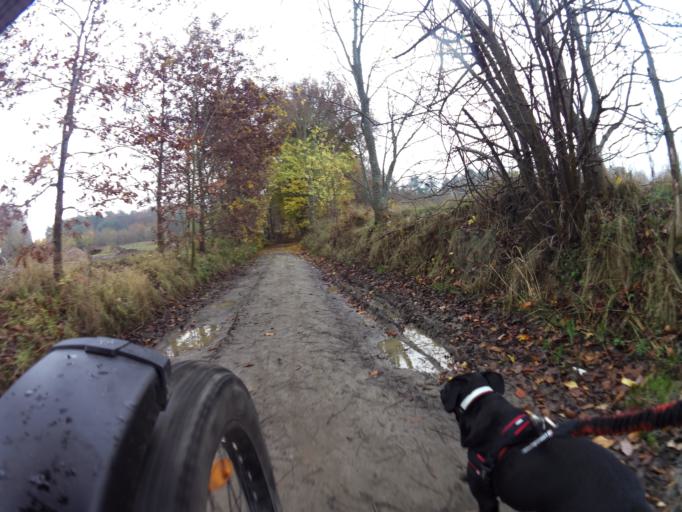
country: PL
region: Pomeranian Voivodeship
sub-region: Powiat pucki
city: Krokowa
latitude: 54.7833
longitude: 18.0875
